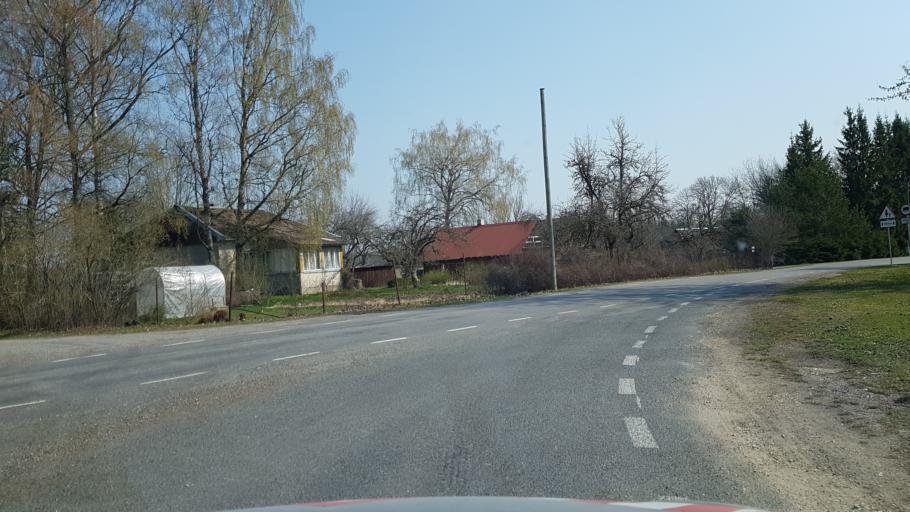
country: EE
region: Raplamaa
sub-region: Kehtna vald
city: Kehtna
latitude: 59.0608
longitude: 24.9541
